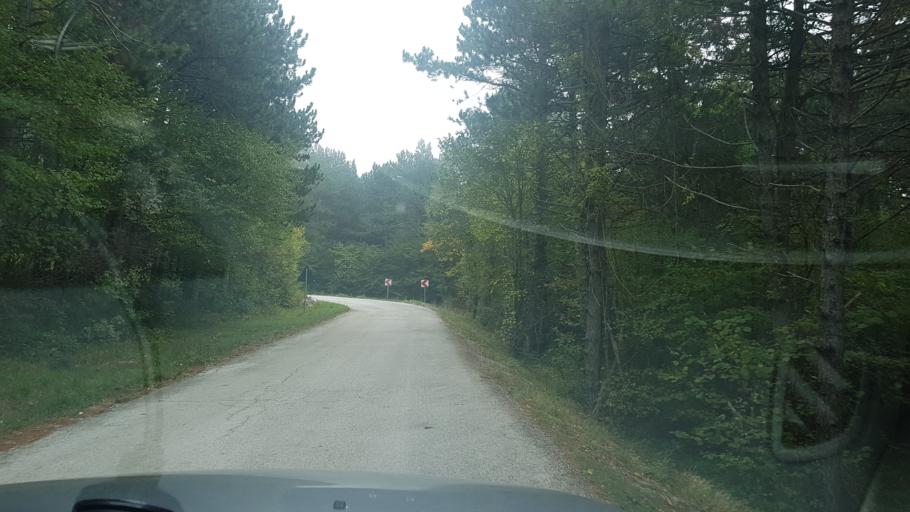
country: HR
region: Istarska
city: Buzet
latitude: 45.4509
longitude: 14.0177
